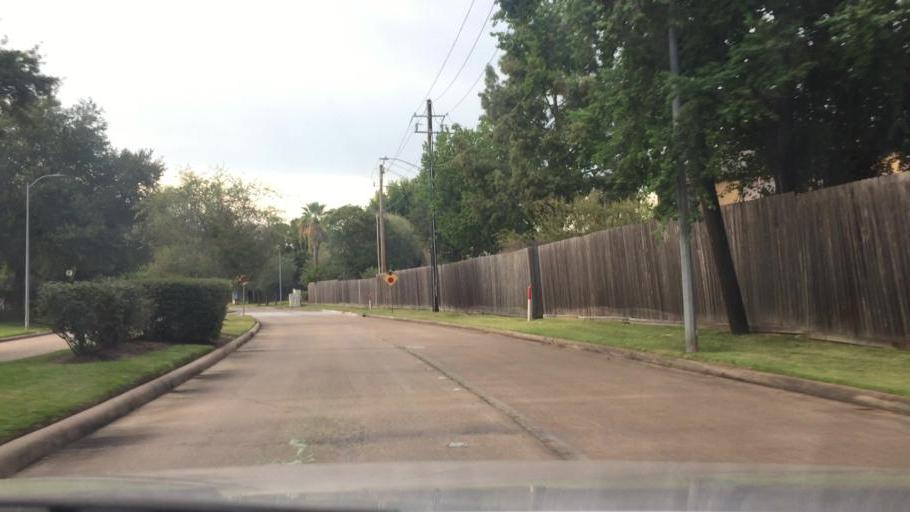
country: US
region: Texas
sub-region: Harris County
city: Bunker Hill Village
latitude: 29.7399
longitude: -95.5813
